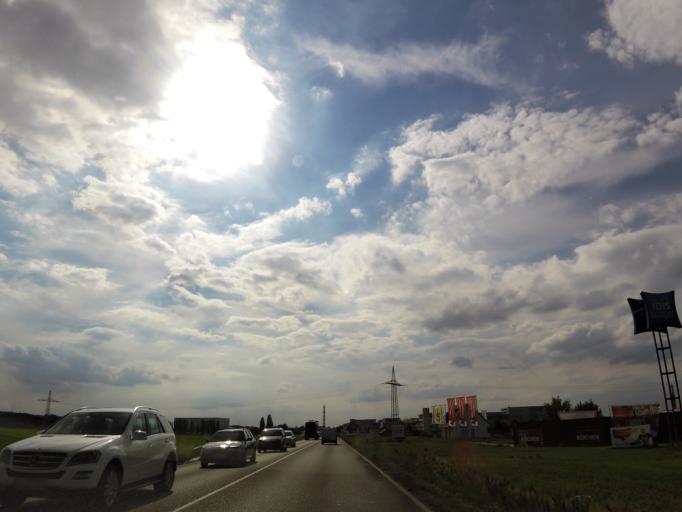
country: DE
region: Saxony-Anhalt
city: Gunthersdorf
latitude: 51.3485
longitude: 12.2019
